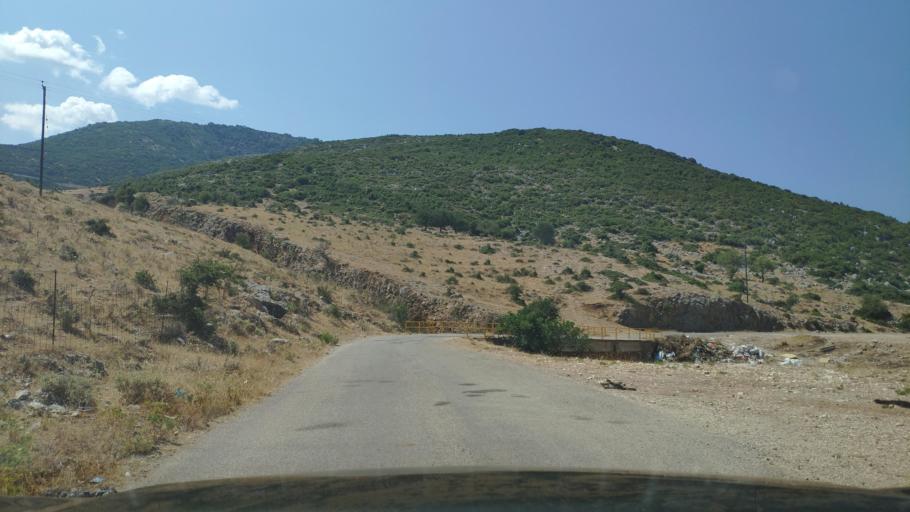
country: GR
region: West Greece
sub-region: Nomos Aitolias kai Akarnanias
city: Monastirakion
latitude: 38.8445
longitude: 20.9429
